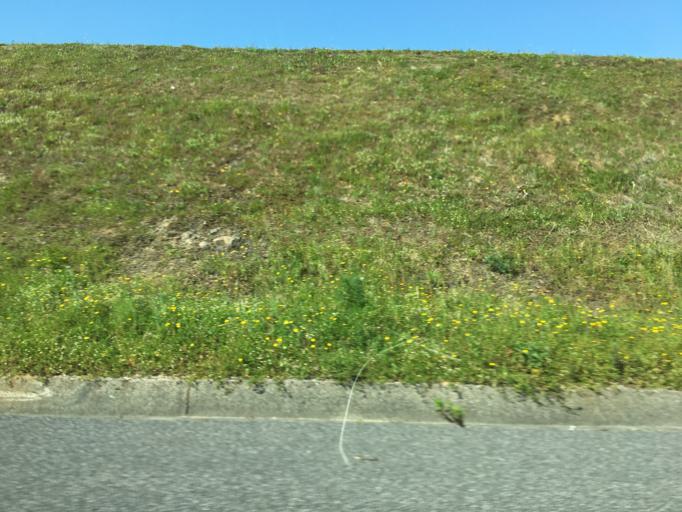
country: PT
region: Lisbon
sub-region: Sintra
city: Rio de Mouro
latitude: 38.8010
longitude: -9.3064
